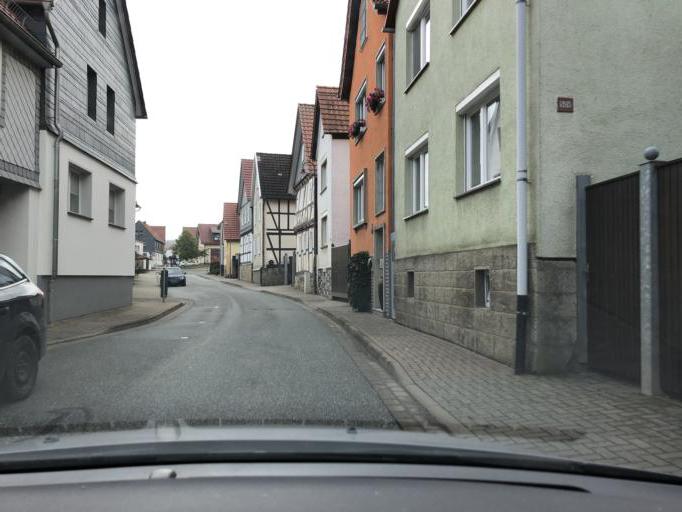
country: DE
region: Thuringia
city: Heuthen
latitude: 51.3328
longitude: 10.2237
